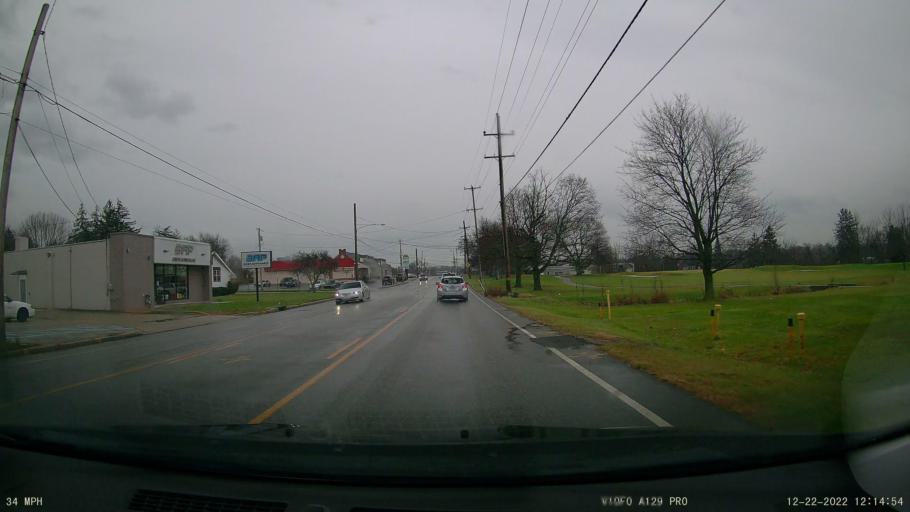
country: US
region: Pennsylvania
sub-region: Montgomery County
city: West Norriton
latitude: 40.1373
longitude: -75.3837
